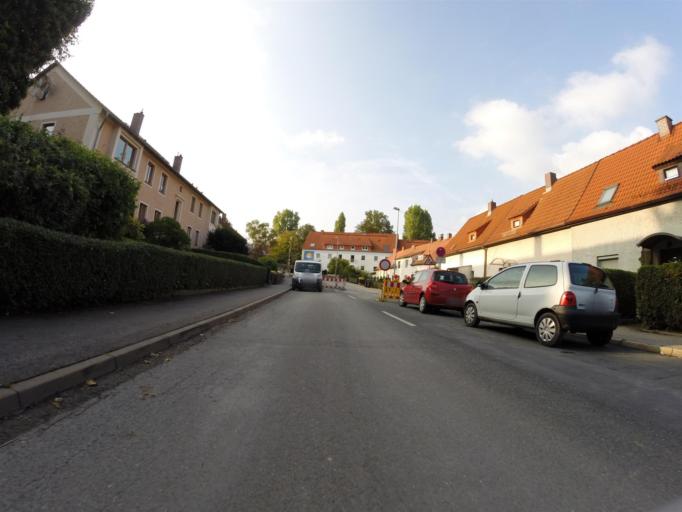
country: DE
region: Thuringia
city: Jena
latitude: 50.9134
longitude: 11.5721
